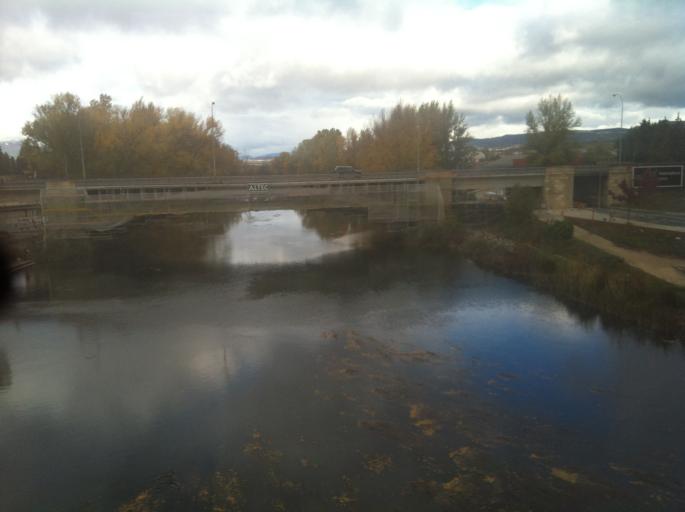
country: ES
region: Castille and Leon
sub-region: Provincia de Burgos
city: Miranda de Ebro
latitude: 42.6869
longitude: -2.9542
